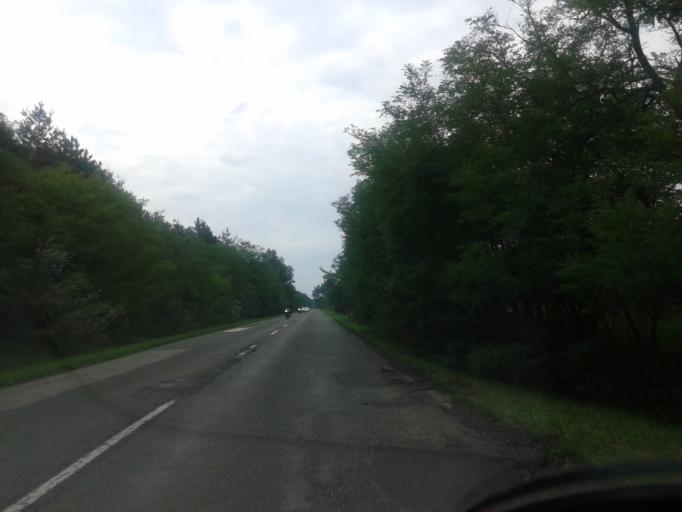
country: HU
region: Csongrad
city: Ruzsa
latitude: 46.2371
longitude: 19.7191
